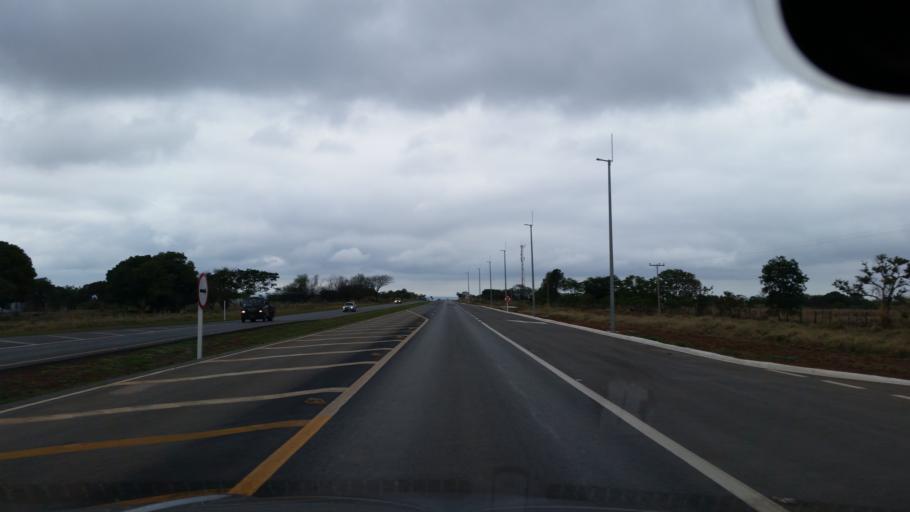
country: BR
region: Goias
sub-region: Luziania
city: Luziania
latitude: -16.4561
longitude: -47.8076
